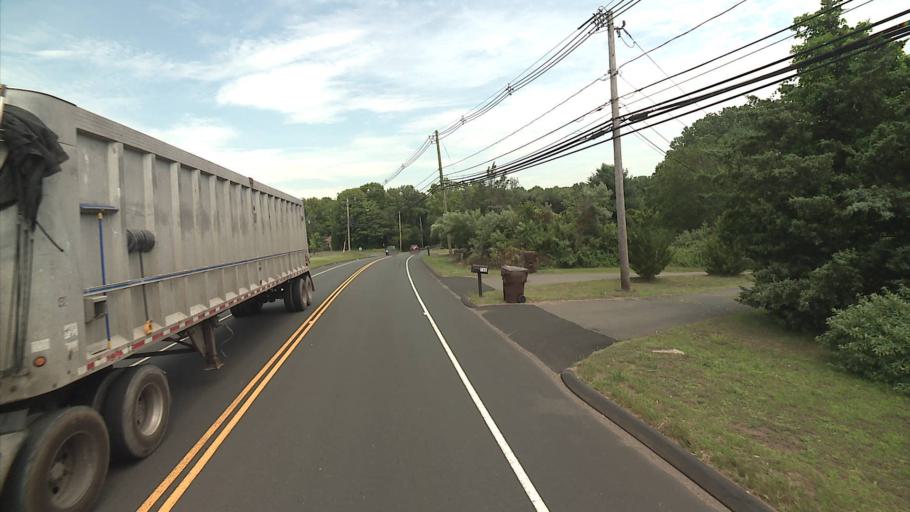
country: US
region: Connecticut
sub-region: New Haven County
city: North Branford
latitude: 41.3842
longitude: -72.7947
